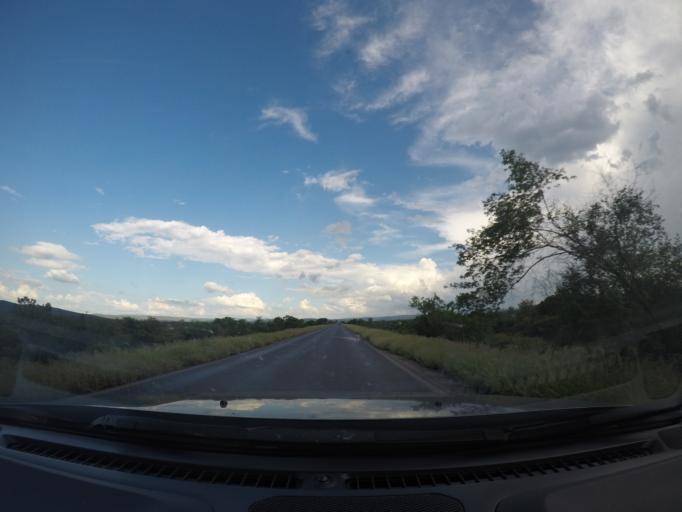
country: BR
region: Bahia
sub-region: Ibotirama
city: Ibotirama
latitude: -12.1591
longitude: -43.2953
